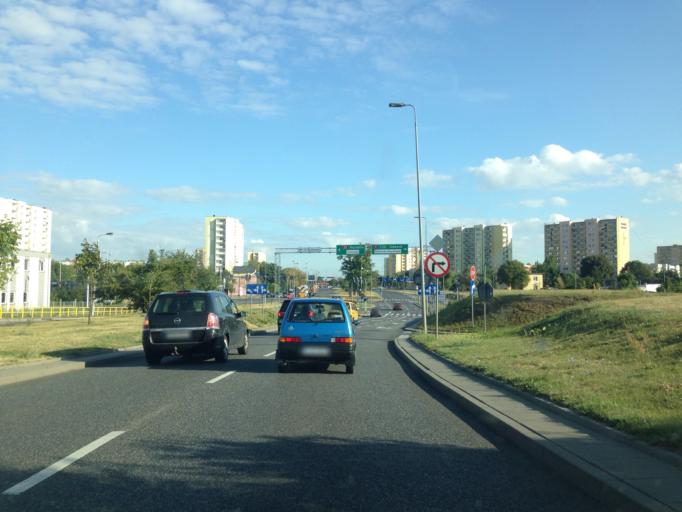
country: PL
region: Kujawsko-Pomorskie
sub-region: Bydgoszcz
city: Bydgoszcz
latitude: 53.1068
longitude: 18.0083
